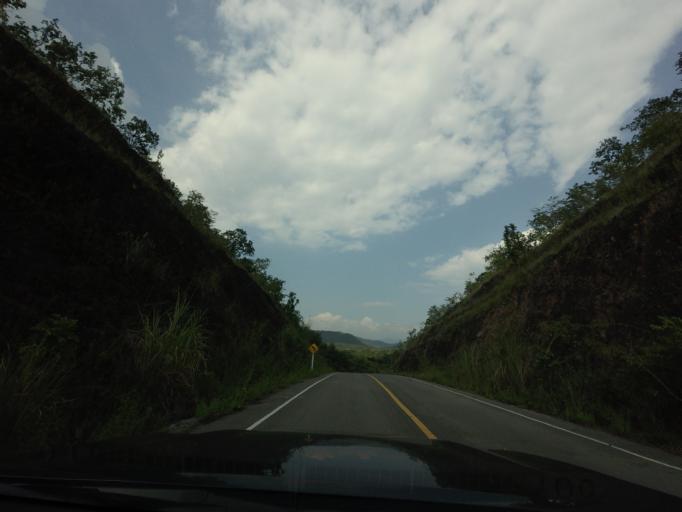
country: TH
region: Nan
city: Na Noi
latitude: 18.3044
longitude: 100.9047
